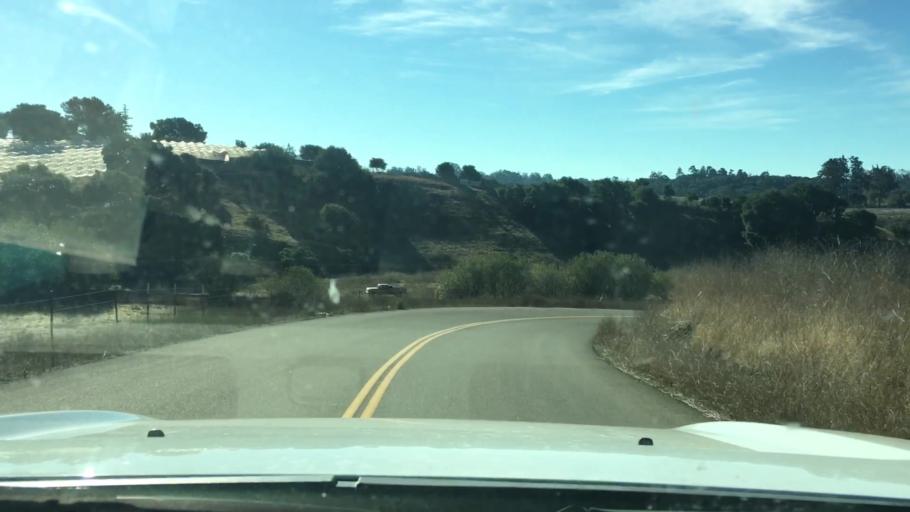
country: US
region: California
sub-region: San Luis Obispo County
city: Arroyo Grande
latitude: 35.0962
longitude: -120.5609
